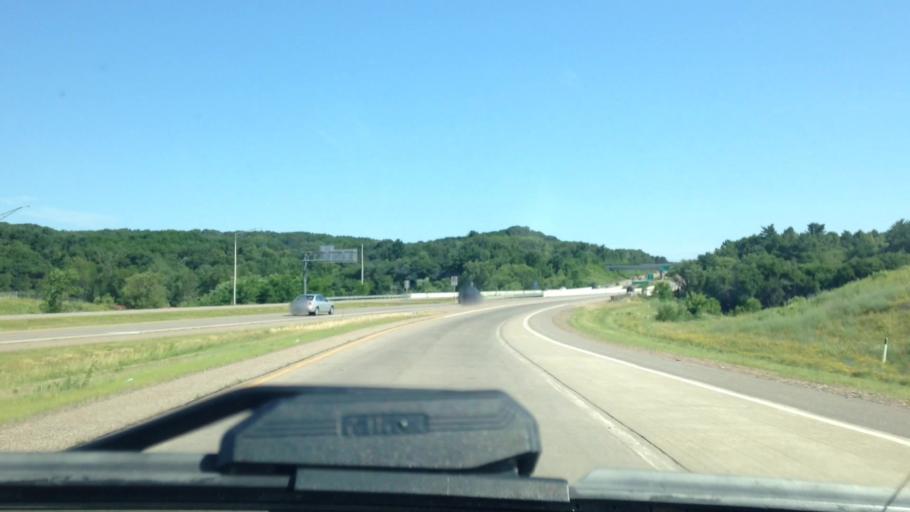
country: US
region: Wisconsin
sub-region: Eau Claire County
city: Altoona
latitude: 44.8201
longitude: -91.4538
